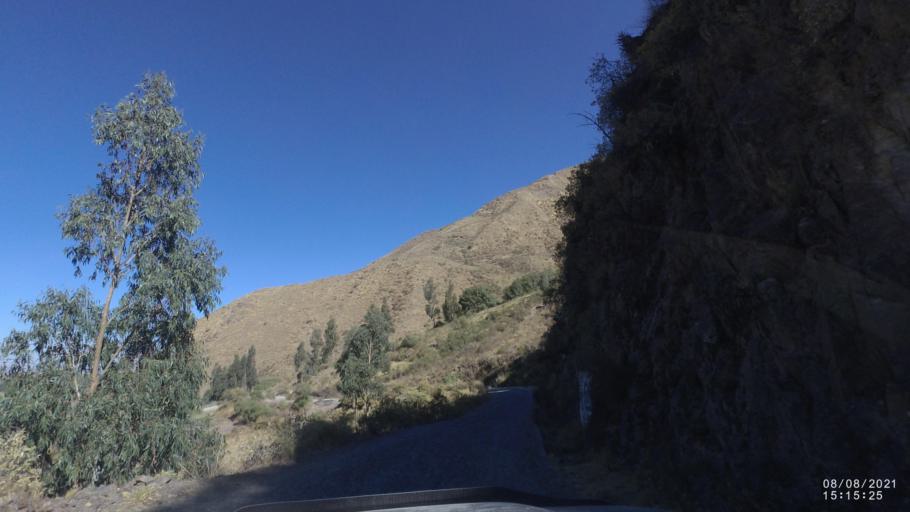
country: BO
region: Cochabamba
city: Sipe Sipe
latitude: -17.2834
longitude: -66.3093
